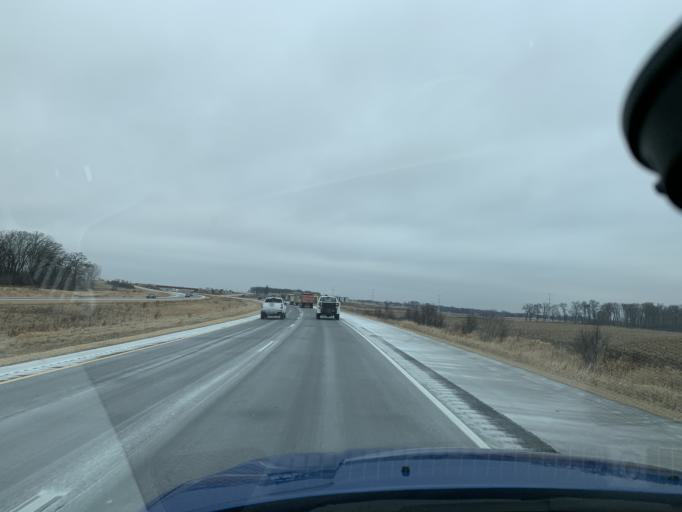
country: US
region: Wisconsin
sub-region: Columbia County
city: Columbus
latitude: 43.3089
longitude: -89.0466
